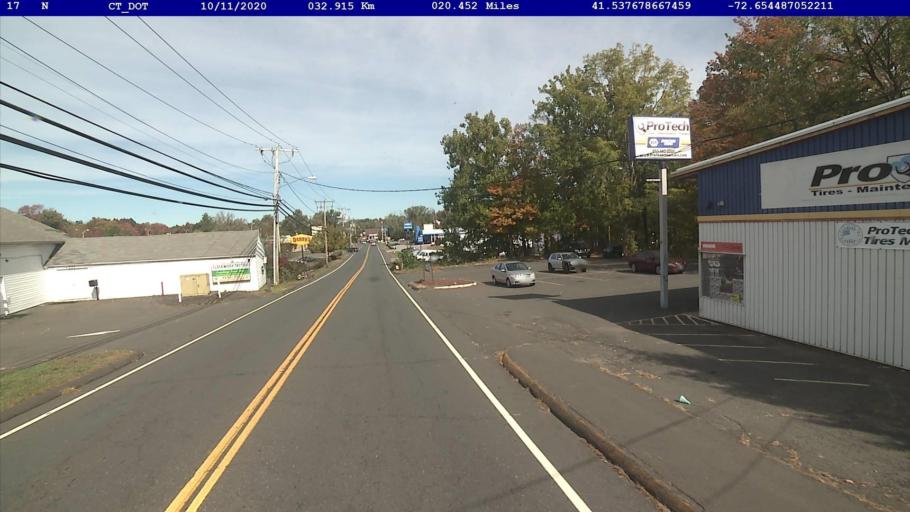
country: US
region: Connecticut
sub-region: Middlesex County
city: Middletown
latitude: 41.5377
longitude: -72.6545
